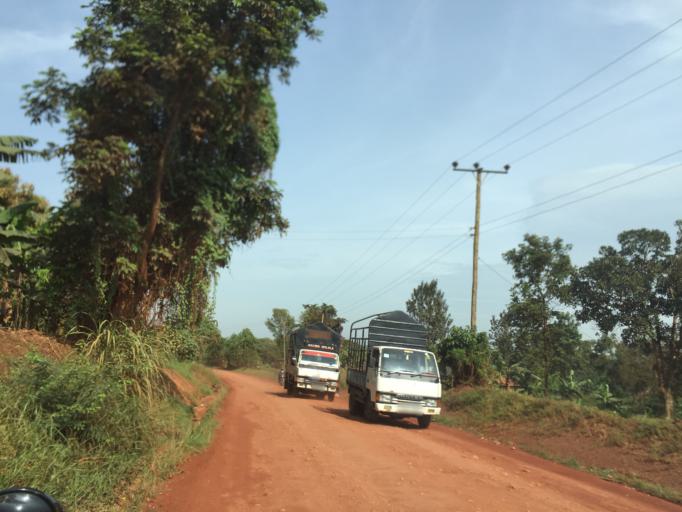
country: UG
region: Central Region
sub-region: Wakiso District
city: Wakiso
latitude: 0.4663
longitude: 32.5397
